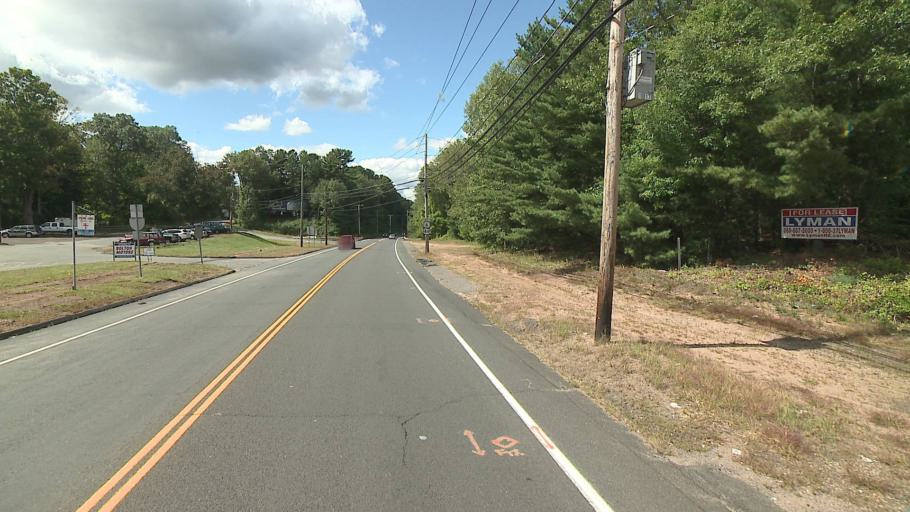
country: US
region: Connecticut
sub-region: Hartford County
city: Manchester
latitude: 41.7839
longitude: -72.4661
